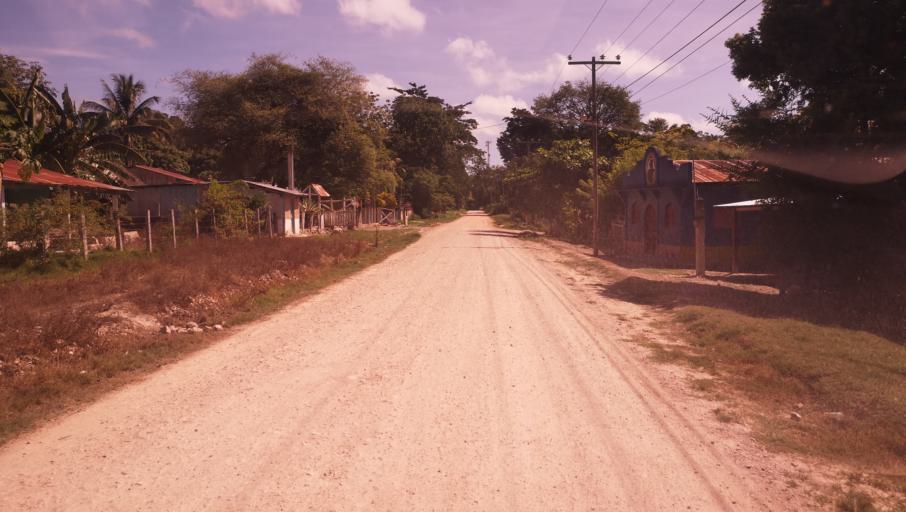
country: GT
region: Peten
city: Melchor de Mencos
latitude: 16.8383
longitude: -89.2998
